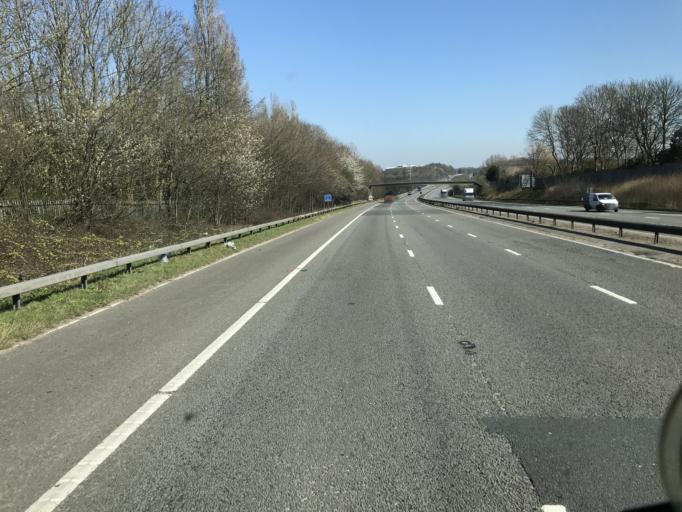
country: GB
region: England
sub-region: Borough of Halton
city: Daresbury
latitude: 53.3197
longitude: -2.6578
